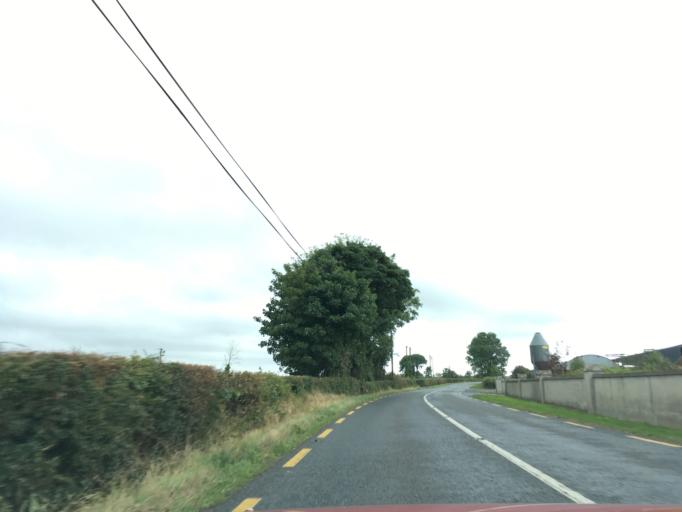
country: IE
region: Munster
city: Fethard
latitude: 52.4273
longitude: -7.7764
